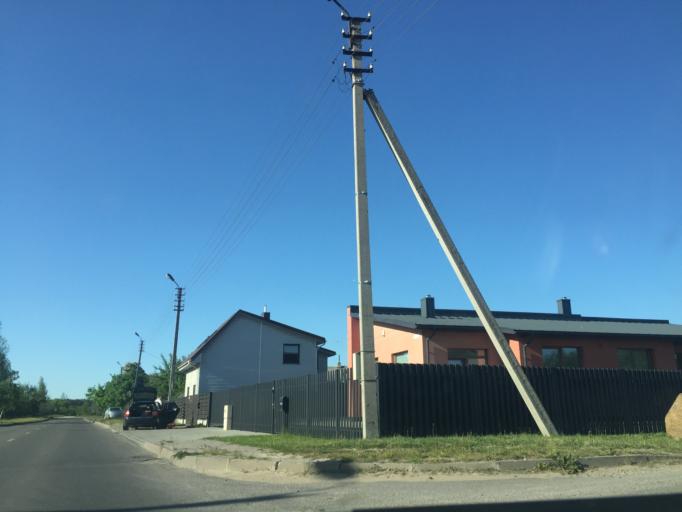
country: LT
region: Panevezys
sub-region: Panevezys City
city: Panevezys
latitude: 55.7484
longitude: 24.3417
